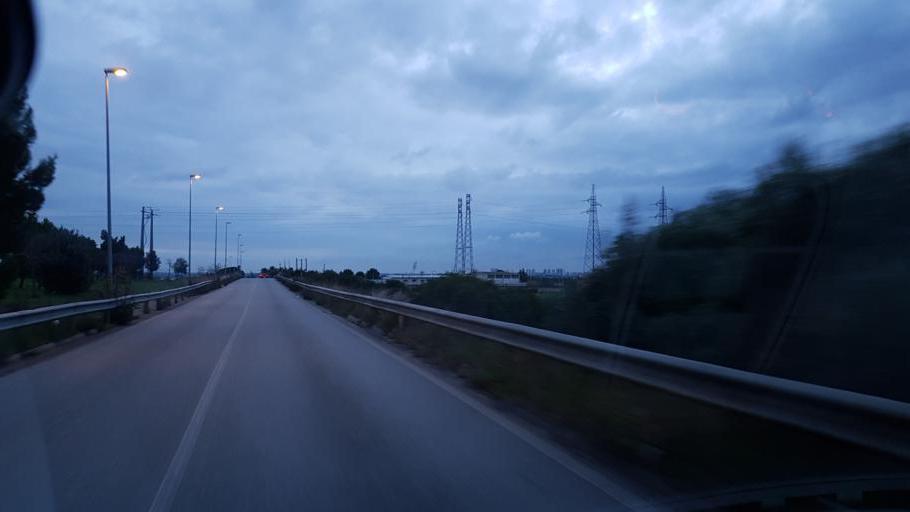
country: IT
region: Apulia
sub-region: Provincia di Taranto
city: Paolo VI
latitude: 40.5163
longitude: 17.2879
